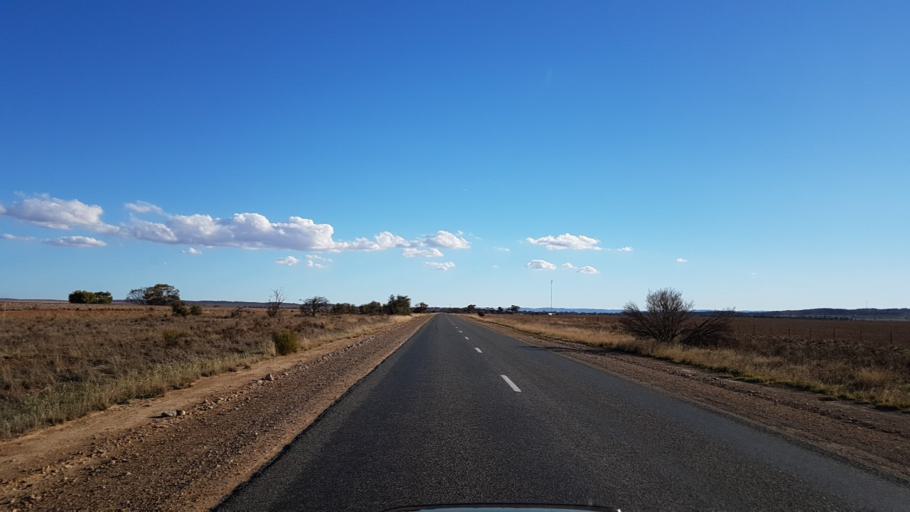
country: AU
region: South Australia
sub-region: Peterborough
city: Peterborough
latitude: -32.9645
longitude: 138.8803
